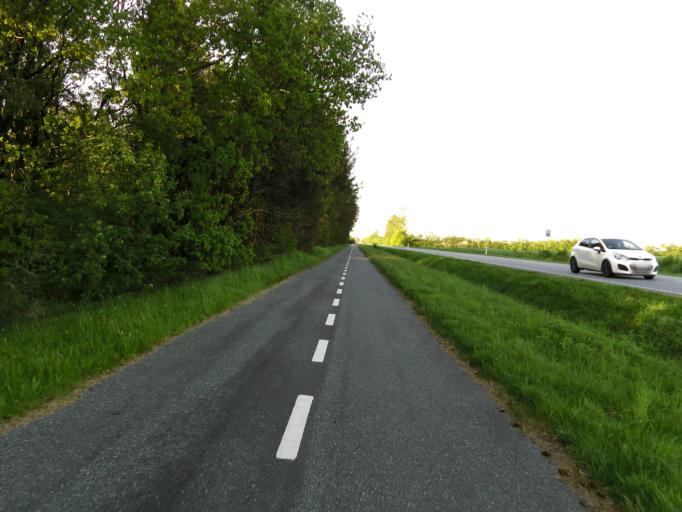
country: DK
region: South Denmark
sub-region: Esbjerg Kommune
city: Ribe
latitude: 55.2977
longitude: 8.7412
